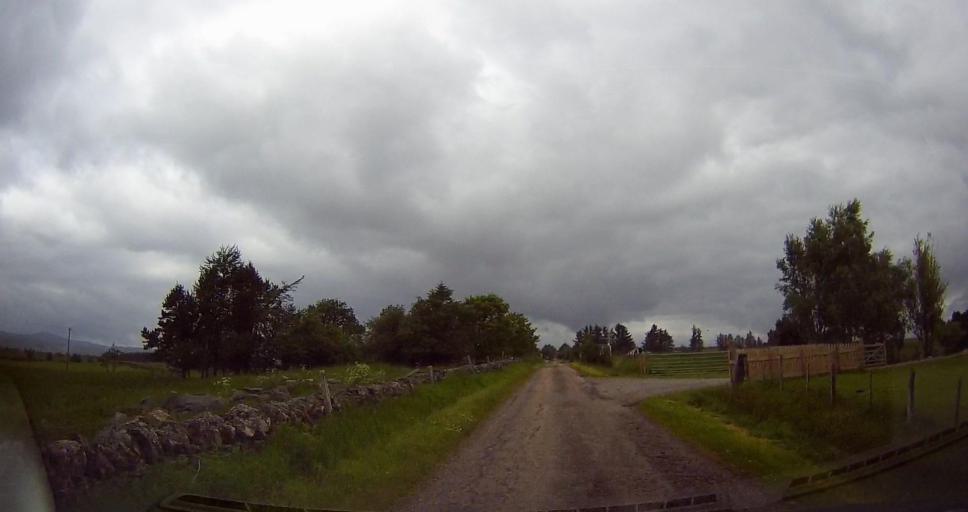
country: GB
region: Scotland
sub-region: Highland
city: Alness
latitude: 58.0723
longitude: -4.4357
